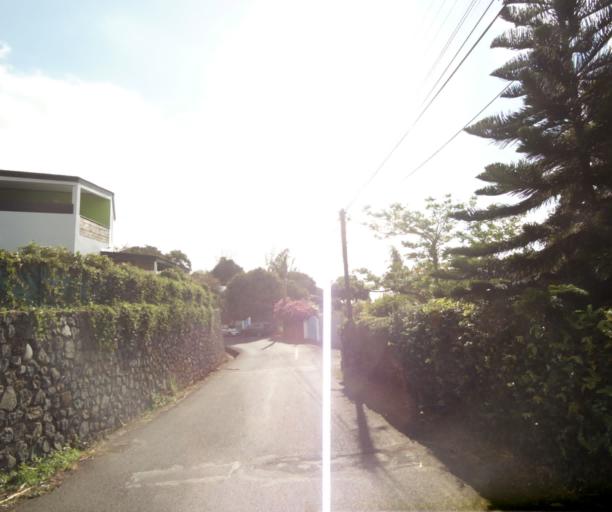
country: RE
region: Reunion
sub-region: Reunion
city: Saint-Paul
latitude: -20.9971
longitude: 55.3313
